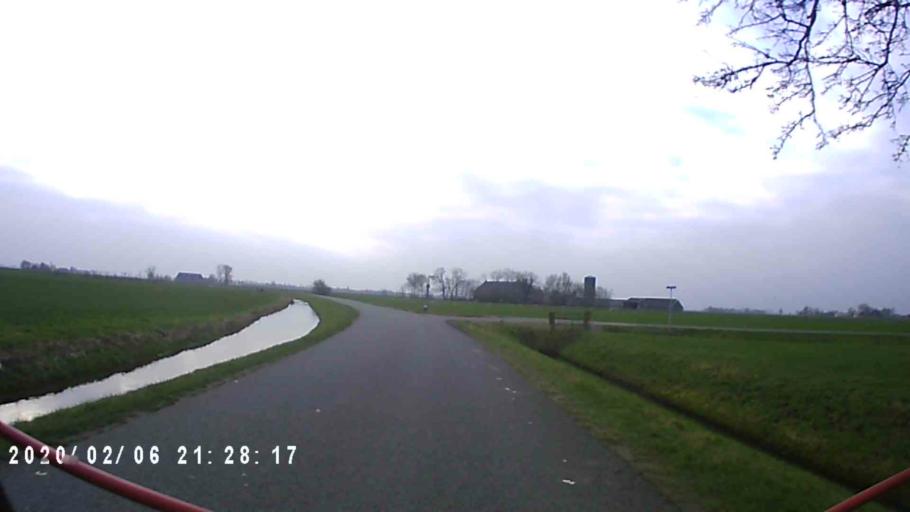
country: NL
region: Groningen
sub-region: Gemeente Zuidhorn
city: Noordhorn
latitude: 53.2804
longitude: 6.3782
